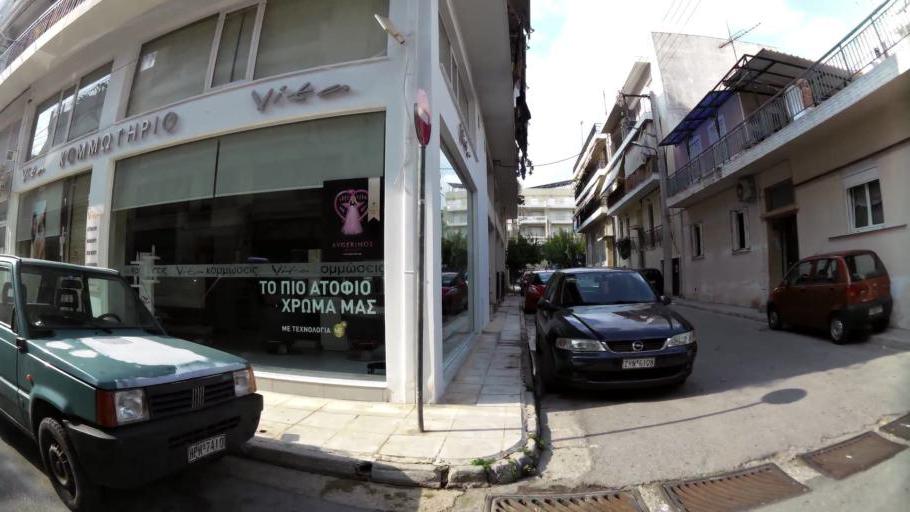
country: GR
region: Attica
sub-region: Nomarchia Athinas
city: Ilion
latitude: 38.0424
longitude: 23.7002
